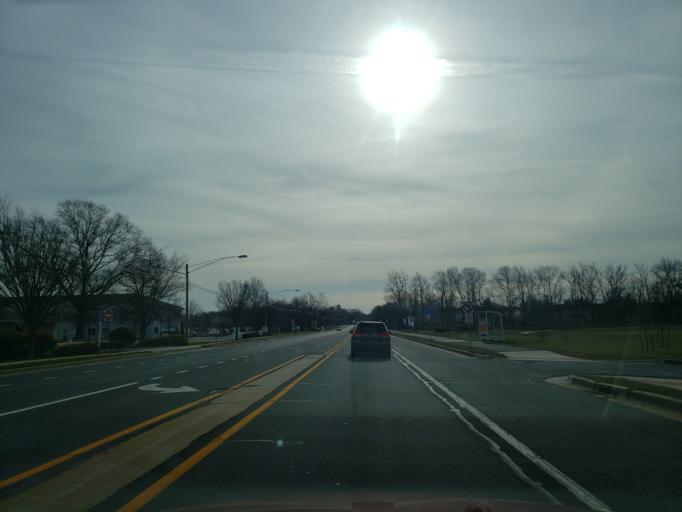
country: US
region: Delaware
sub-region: Kent County
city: Dover
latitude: 39.1759
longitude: -75.5532
